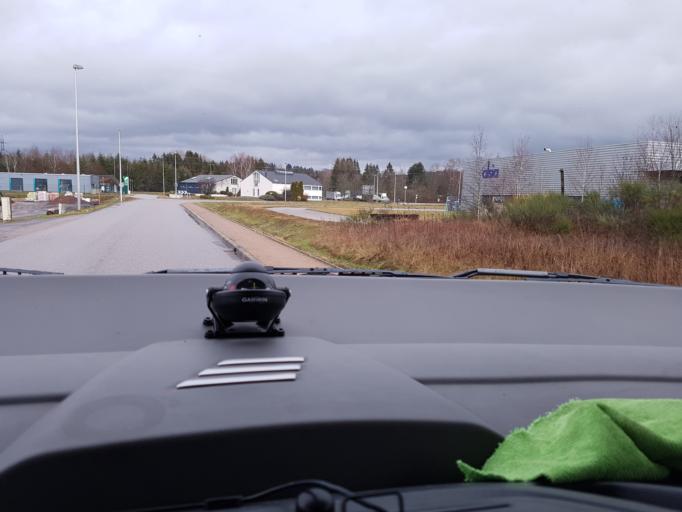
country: FR
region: Lorraine
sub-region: Departement des Vosges
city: Saint-Michel-sur-Meurthe
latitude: 48.3236
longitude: 6.8945
